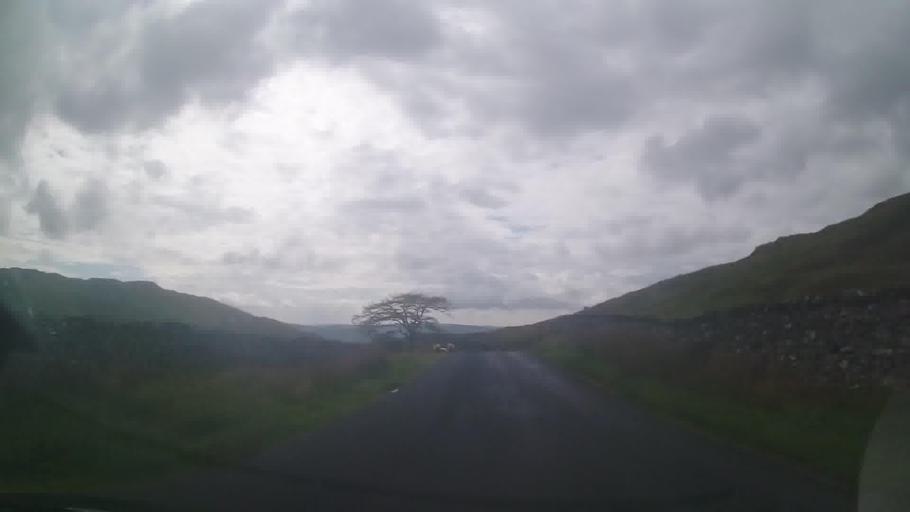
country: GB
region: England
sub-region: Cumbria
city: Ambleside
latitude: 54.4514
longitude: -2.9378
